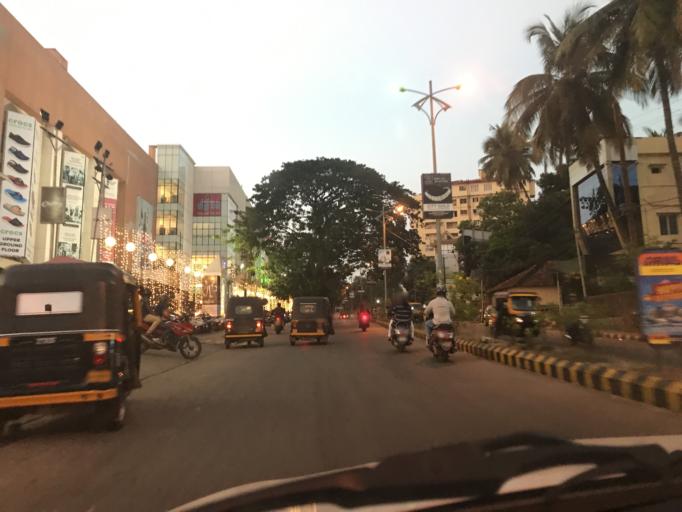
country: IN
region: Karnataka
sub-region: Dakshina Kannada
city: Ullal
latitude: 12.8566
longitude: 74.8393
